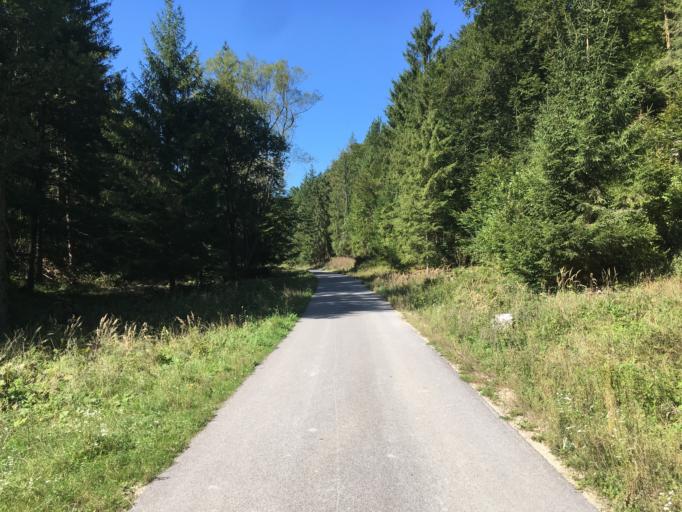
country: SK
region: Trenciansky
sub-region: Okres Povazska Bystrica
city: Povazska Bystrica
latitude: 49.0076
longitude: 18.4553
